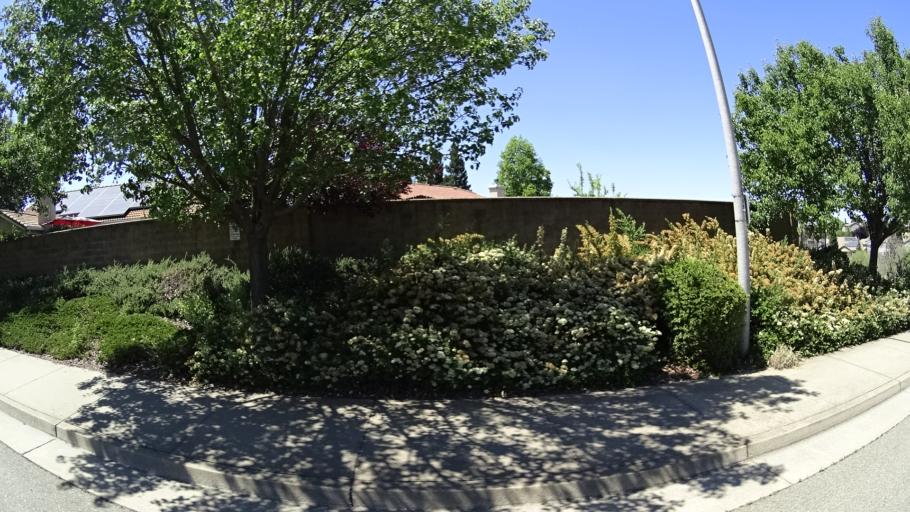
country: US
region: California
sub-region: Placer County
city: Rocklin
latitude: 38.8215
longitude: -121.2721
